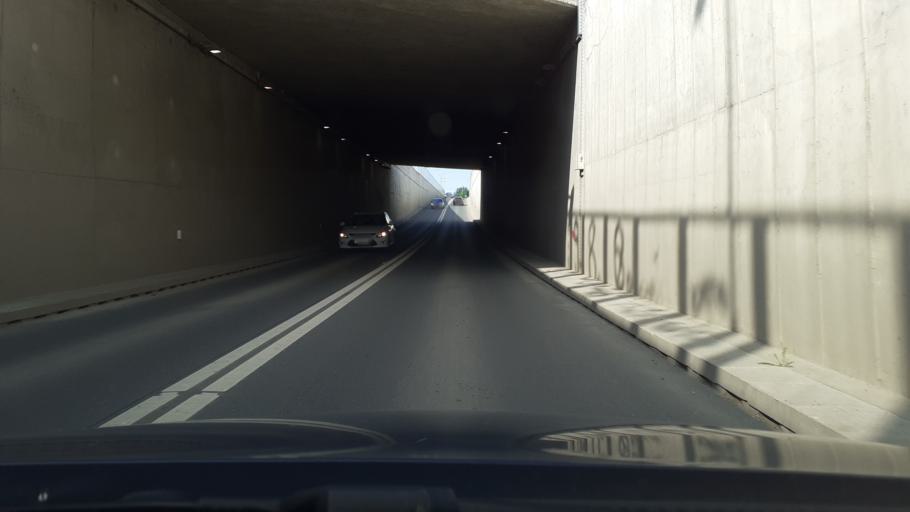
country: HR
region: Brodsko-Posavska
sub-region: Grad Slavonski Brod
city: Slavonski Brod
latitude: 45.1619
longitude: 18.0324
